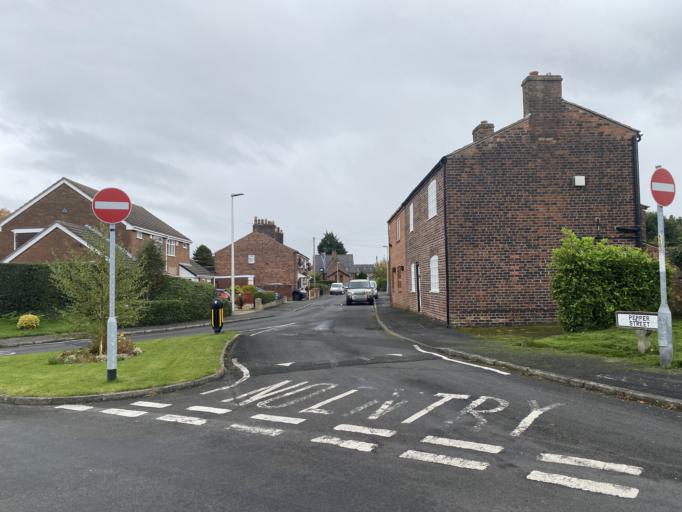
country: GB
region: England
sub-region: Borough of Halton
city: Hale
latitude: 53.3365
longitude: -2.8005
